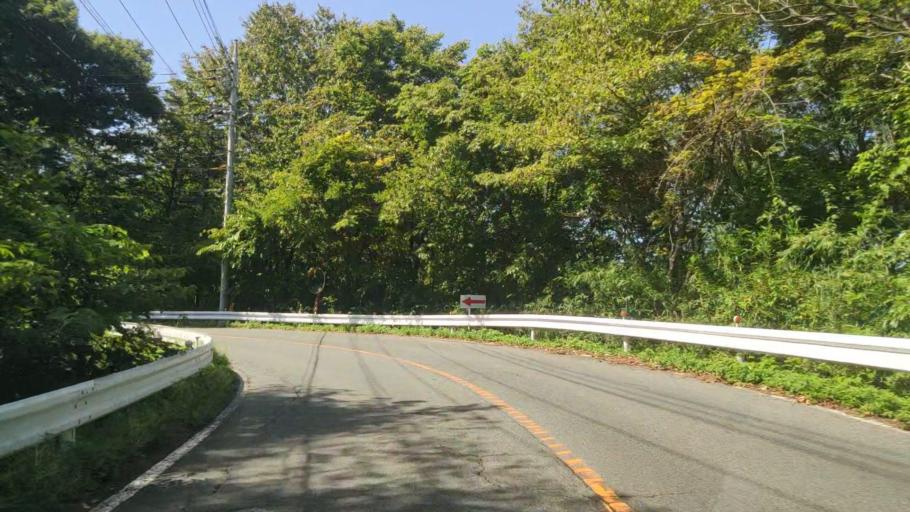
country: JP
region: Gunma
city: Shibukawa
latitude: 36.5013
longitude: 138.9054
